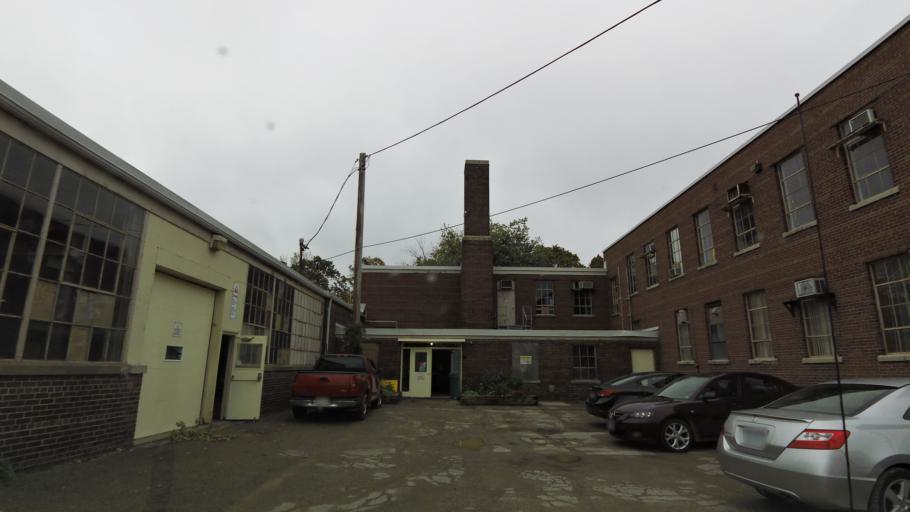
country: CA
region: Ontario
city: Etobicoke
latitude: 43.5837
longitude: -79.5502
